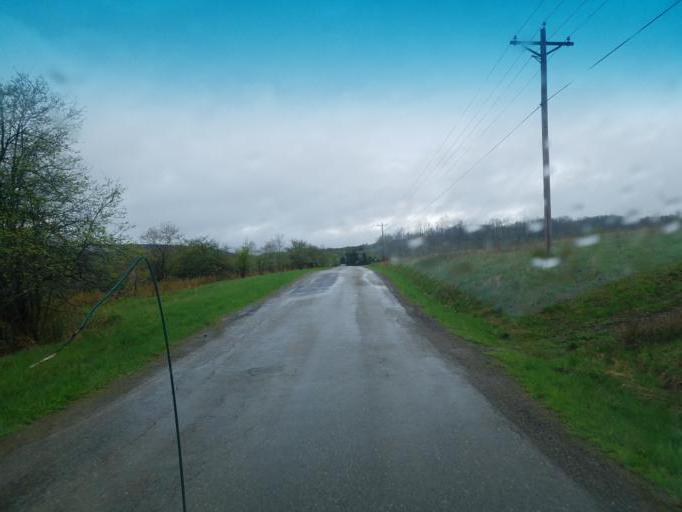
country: US
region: Pennsylvania
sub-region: Tioga County
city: Westfield
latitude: 41.9764
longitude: -77.6743
